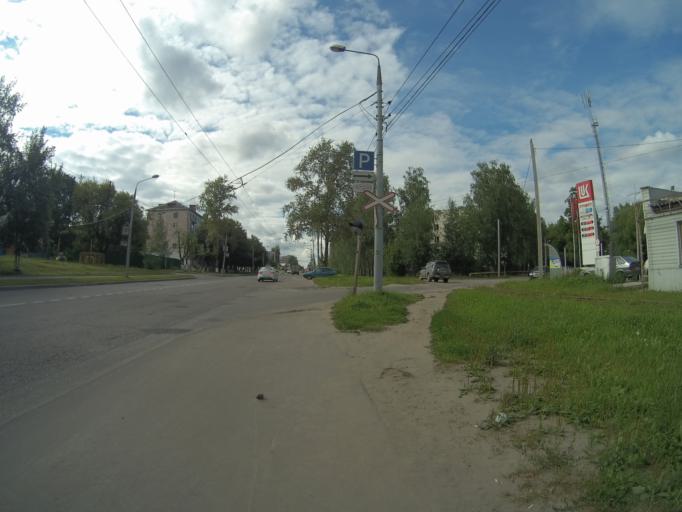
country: RU
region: Vladimir
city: Kommunar
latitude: 56.1461
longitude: 40.4362
